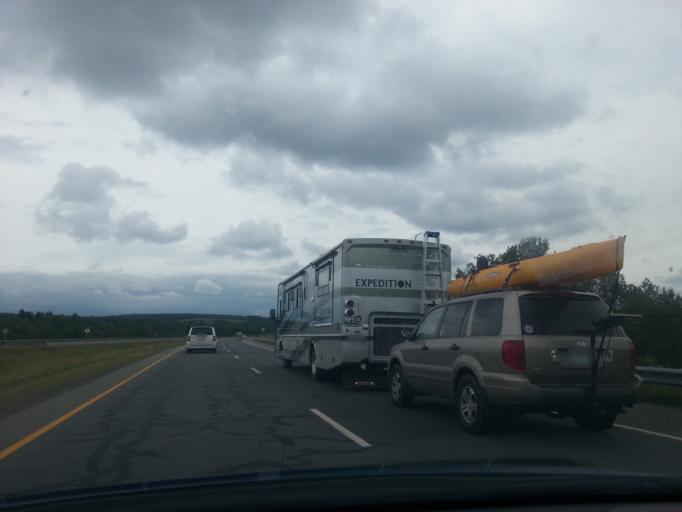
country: US
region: Maine
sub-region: Aroostook County
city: Madawaska
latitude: 47.3299
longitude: -68.1333
